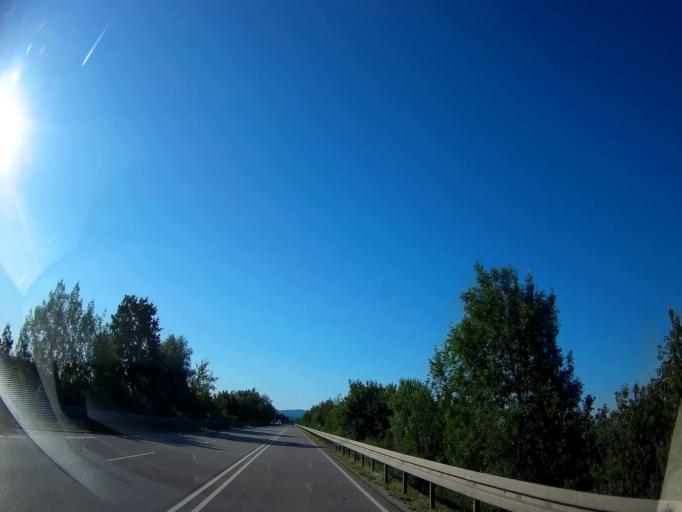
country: DE
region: Bavaria
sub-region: Lower Bavaria
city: Alterhofen
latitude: 48.8739
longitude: 12.6246
